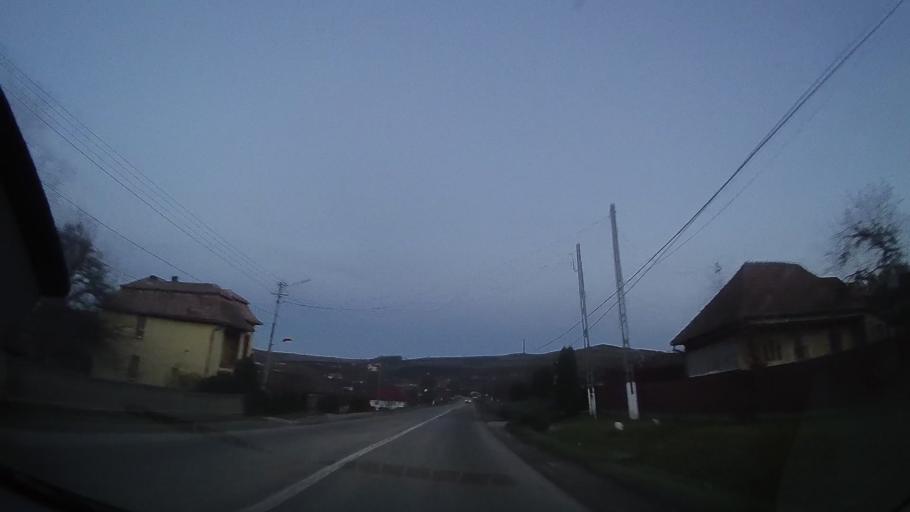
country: RO
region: Cluj
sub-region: Comuna Camarasu
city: Camarasu
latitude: 46.7947
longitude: 24.1328
